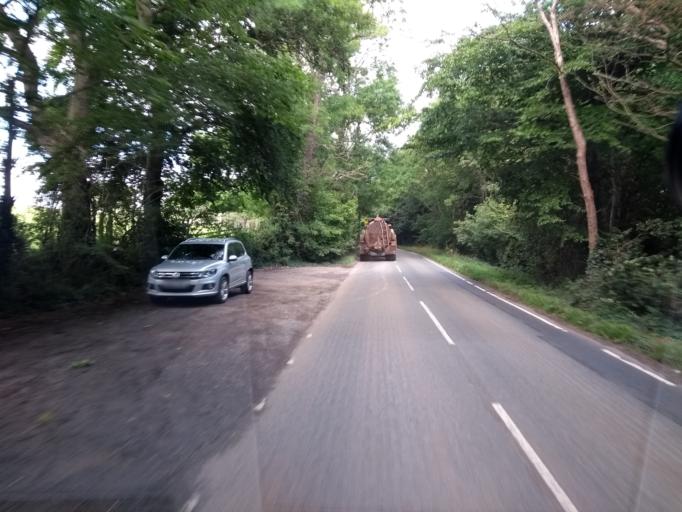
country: GB
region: England
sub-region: Somerset
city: Street
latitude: 51.1050
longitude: -2.7305
